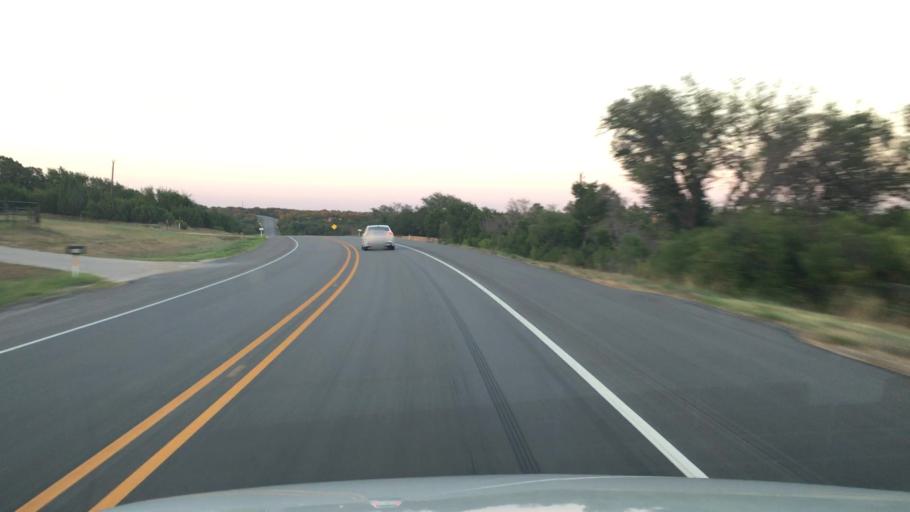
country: US
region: Texas
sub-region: Somervell County
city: Glen Rose
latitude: 32.1909
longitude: -97.8259
